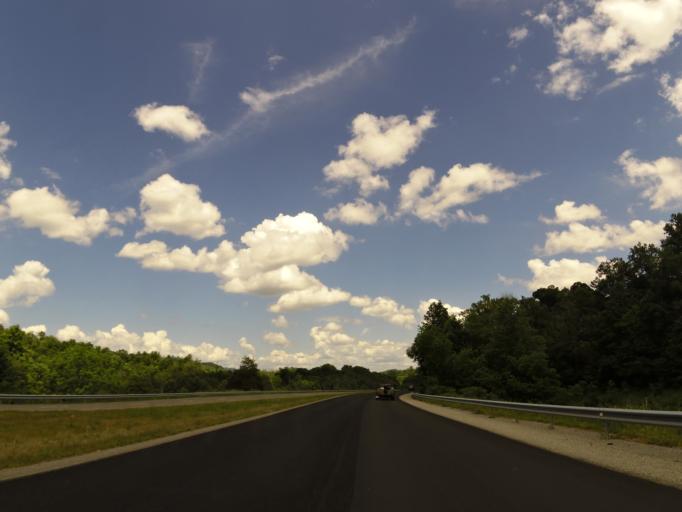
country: US
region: Kentucky
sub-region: Harlan County
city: Harlan
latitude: 36.6921
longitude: -83.2988
